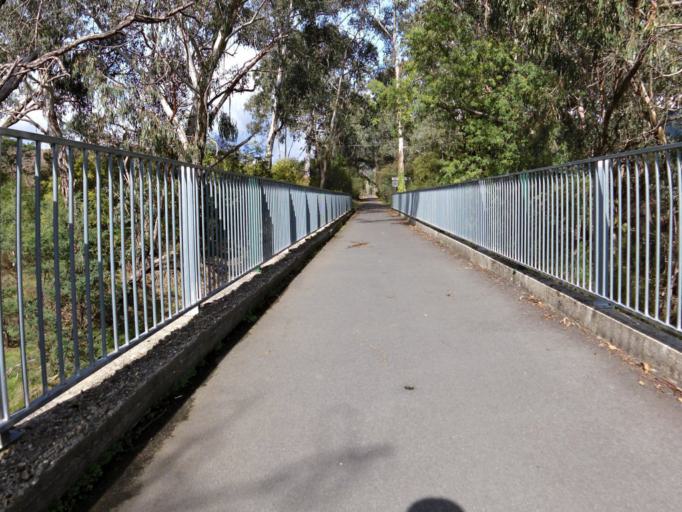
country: AU
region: Victoria
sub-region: Alpine
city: Mount Beauty
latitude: -36.7184
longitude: 146.9439
